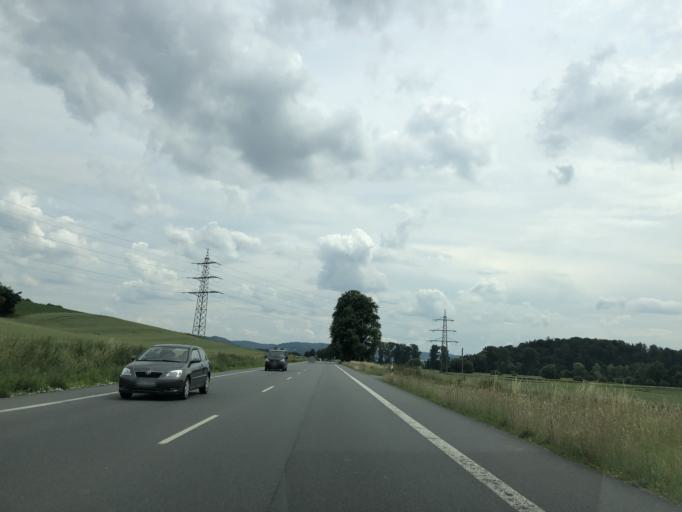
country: DE
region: Hesse
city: Gross-Bieberau
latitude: 49.7953
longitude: 8.8390
